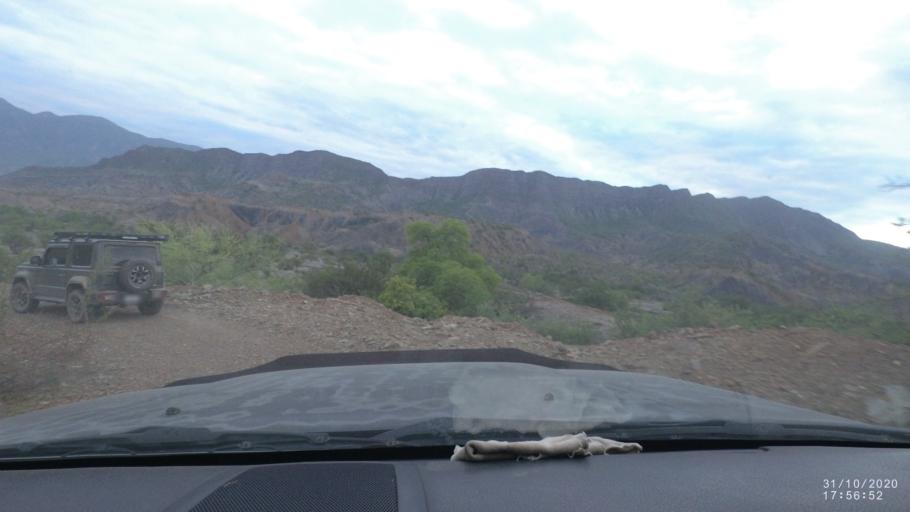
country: BO
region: Chuquisaca
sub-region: Provincia Zudanez
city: Mojocoya
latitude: -18.6483
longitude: -64.5315
